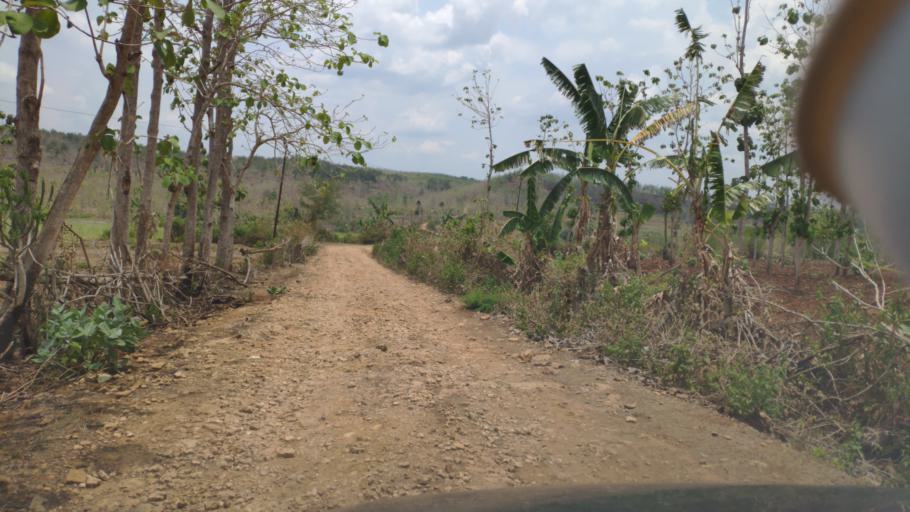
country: ID
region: Central Java
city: Ngapus
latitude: -6.9591
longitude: 111.2187
